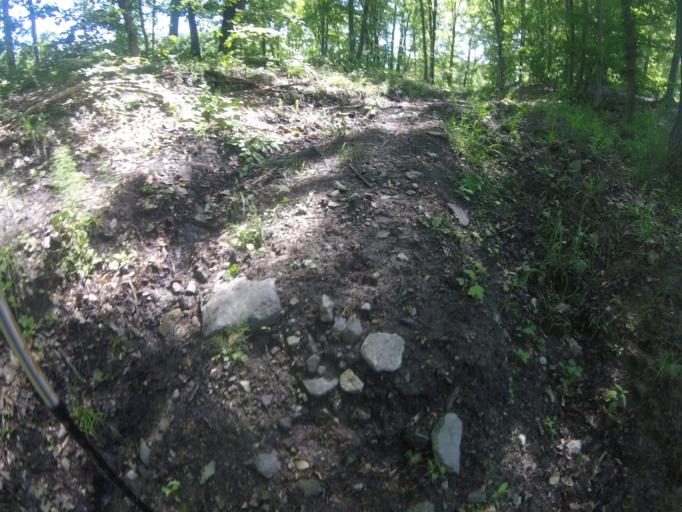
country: HU
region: Nograd
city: Batonyterenye
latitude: 47.9278
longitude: 19.8098
